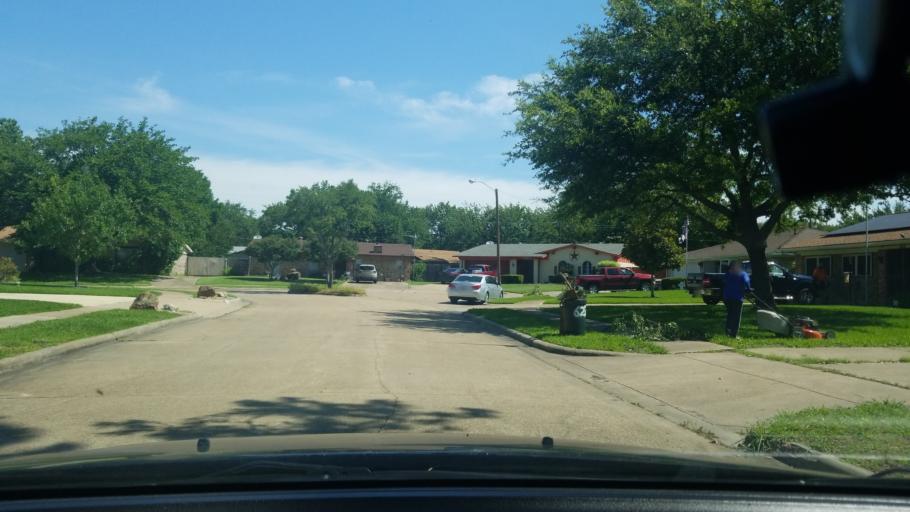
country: US
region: Texas
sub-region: Dallas County
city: Mesquite
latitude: 32.7723
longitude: -96.5951
